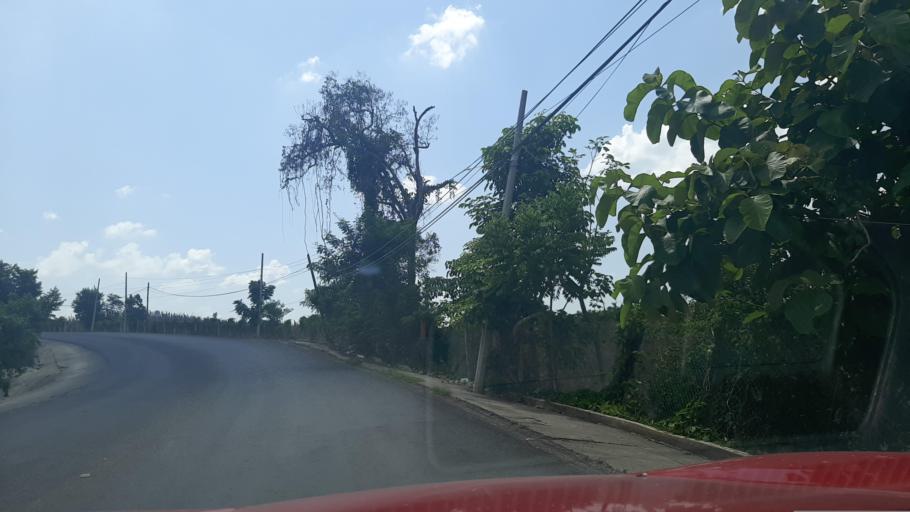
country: MX
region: Veracruz
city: Coatzintla
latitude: 20.4983
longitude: -97.4407
